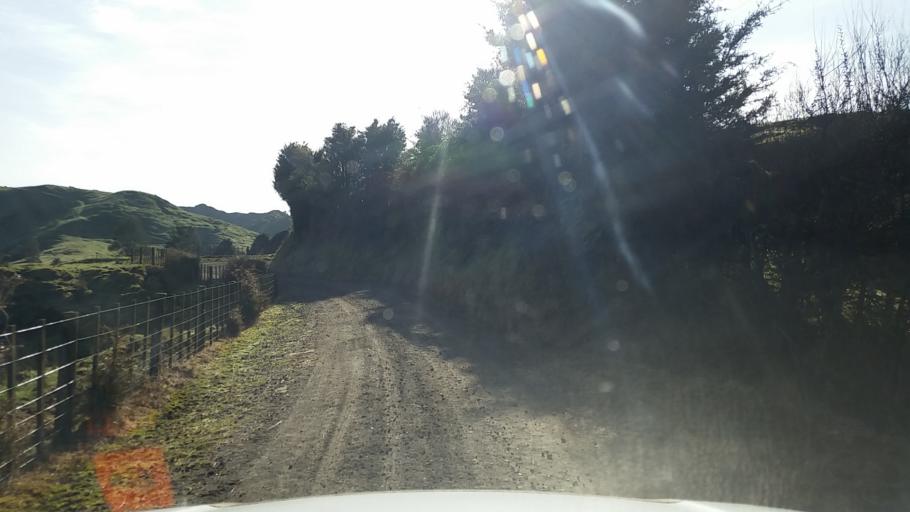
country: NZ
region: Taranaki
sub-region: South Taranaki District
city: Eltham
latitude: -39.3153
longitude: 174.5340
